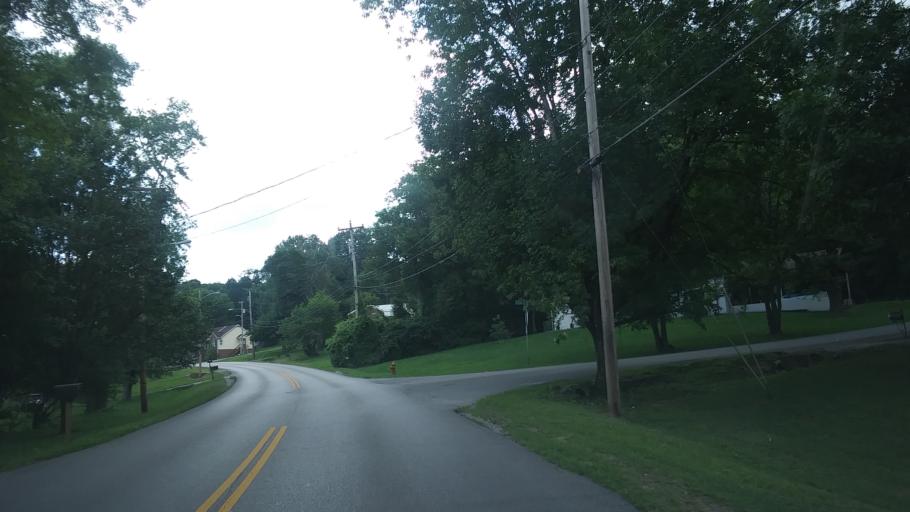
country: US
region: Tennessee
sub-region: Davidson County
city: Oak Hill
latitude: 36.0634
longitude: -86.7026
